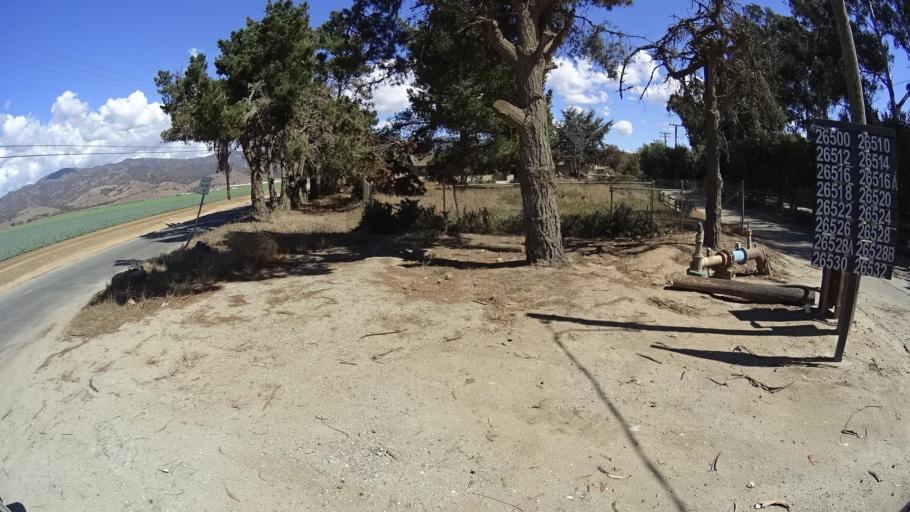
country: US
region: California
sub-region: Monterey County
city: Chualar
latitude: 36.6196
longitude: -121.5081
